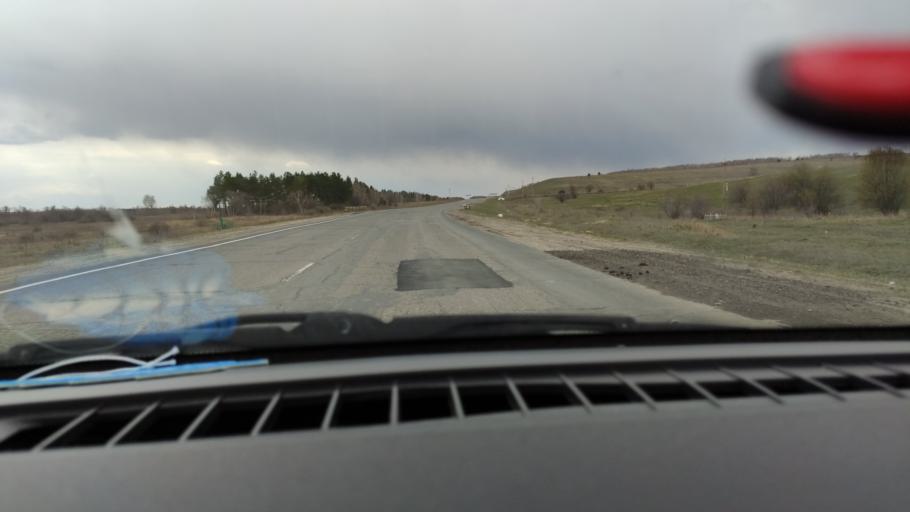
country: RU
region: Saratov
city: Sinodskoye
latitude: 52.0762
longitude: 46.7882
